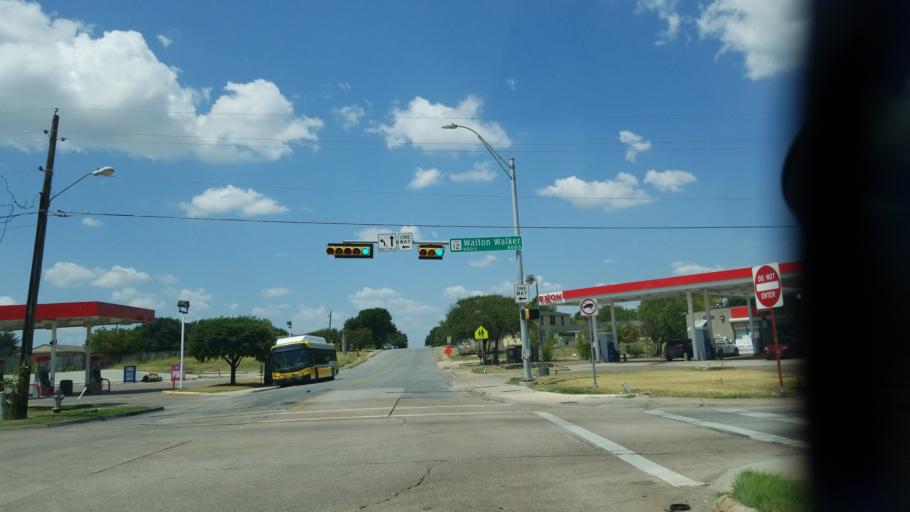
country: US
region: Texas
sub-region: Dallas County
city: Cockrell Hill
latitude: 32.7364
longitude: -96.9202
